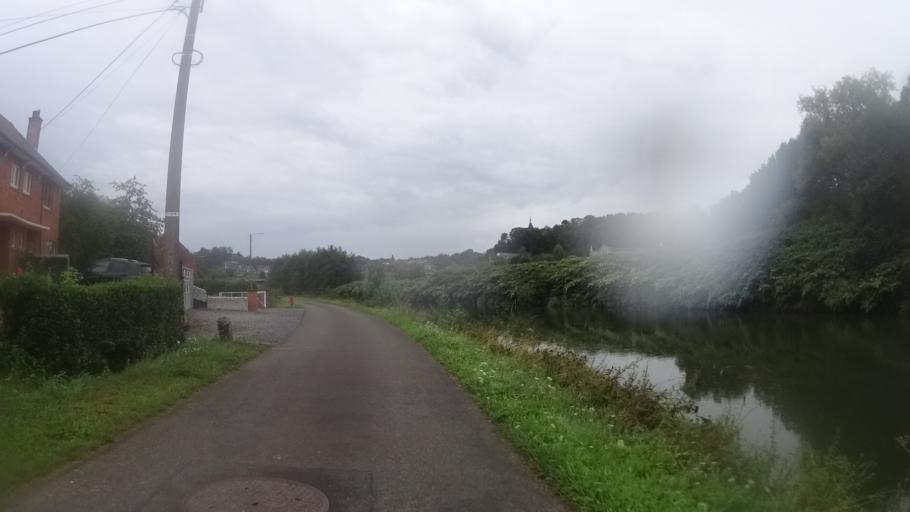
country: BE
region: Wallonia
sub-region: Province du Hainaut
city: Thuin
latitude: 50.3470
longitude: 4.2791
